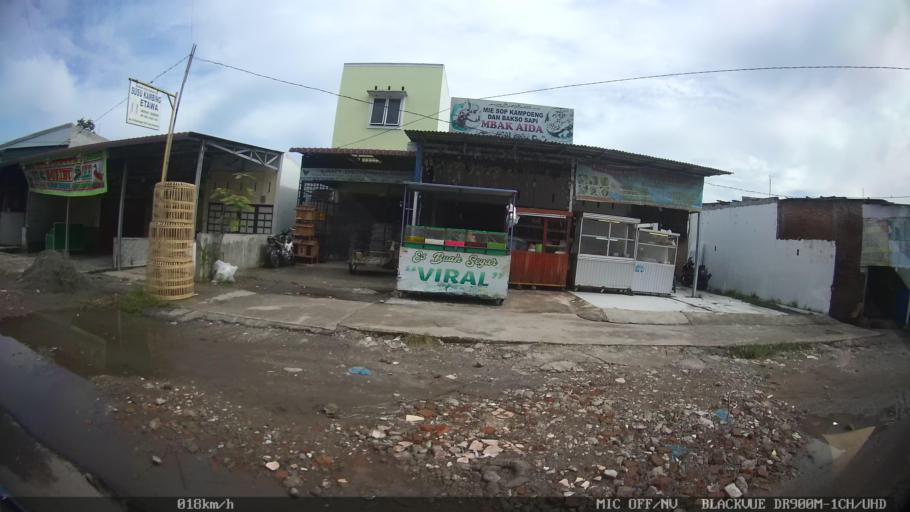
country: ID
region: North Sumatra
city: Medan
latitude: 3.6207
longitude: 98.7282
